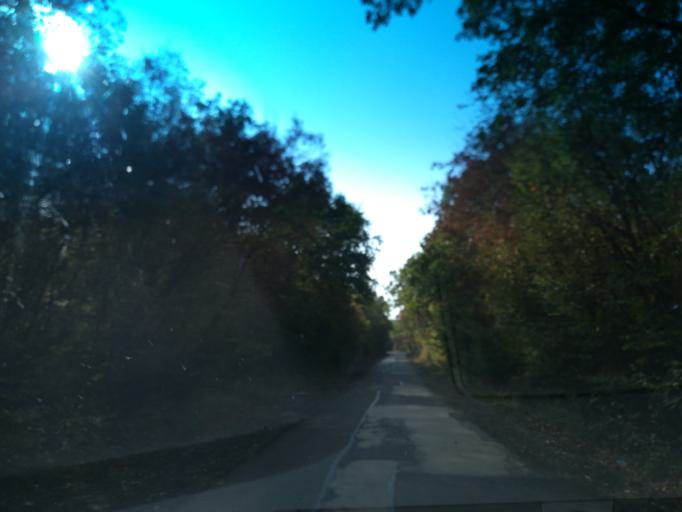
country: BG
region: Stara Zagora
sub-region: Obshtina Nikolaevo
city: Elkhovo
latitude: 42.3254
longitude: 25.3987
